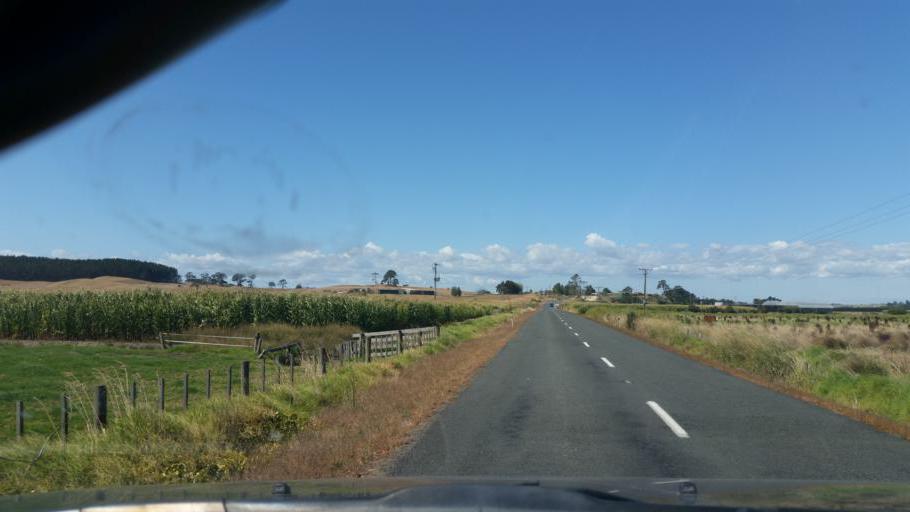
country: NZ
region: Northland
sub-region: Kaipara District
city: Dargaville
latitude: -35.9486
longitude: 173.8052
